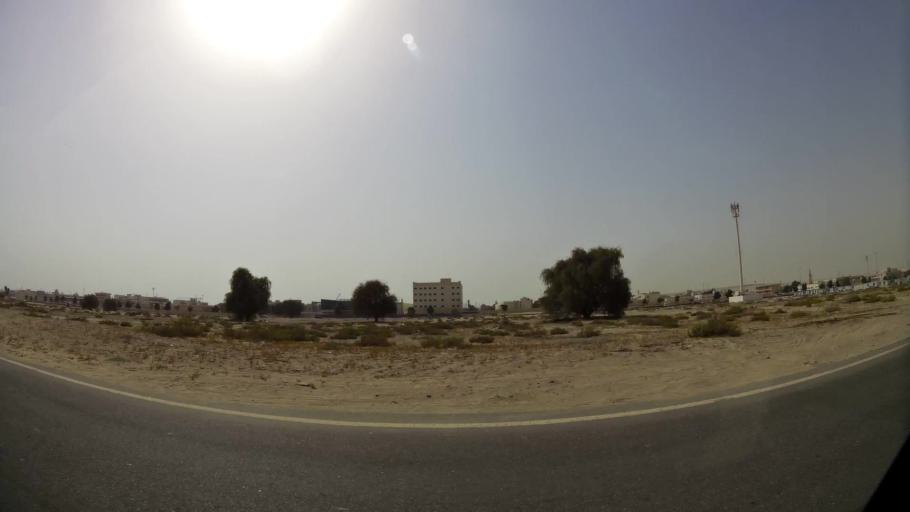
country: AE
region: Ash Shariqah
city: Sharjah
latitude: 25.2638
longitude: 55.4365
